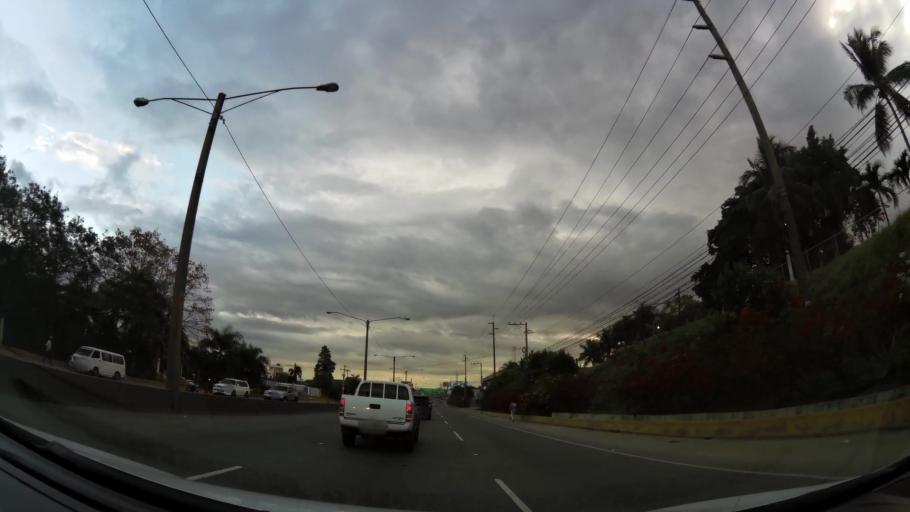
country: DO
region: Santo Domingo
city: Santo Domingo Oeste
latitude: 18.5282
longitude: -70.0112
